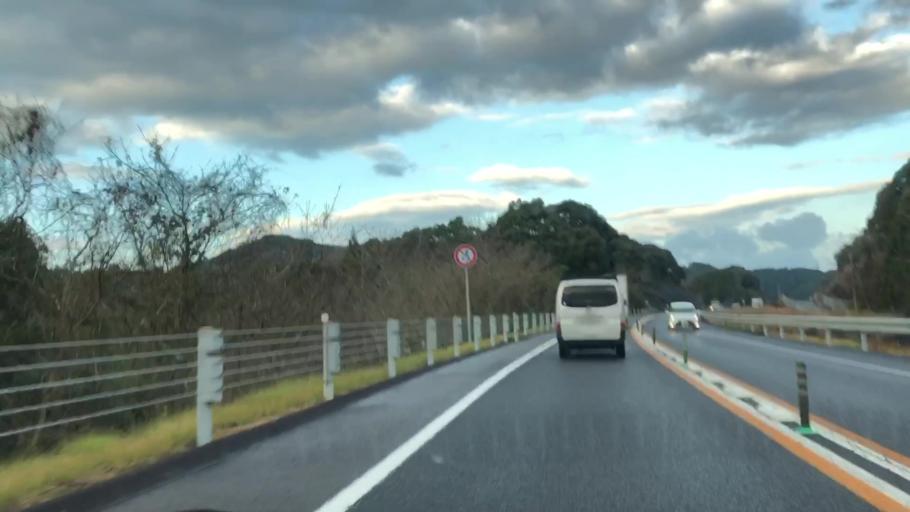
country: JP
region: Saga Prefecture
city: Ureshinomachi-shimojuku
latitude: 33.1438
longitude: 129.9543
